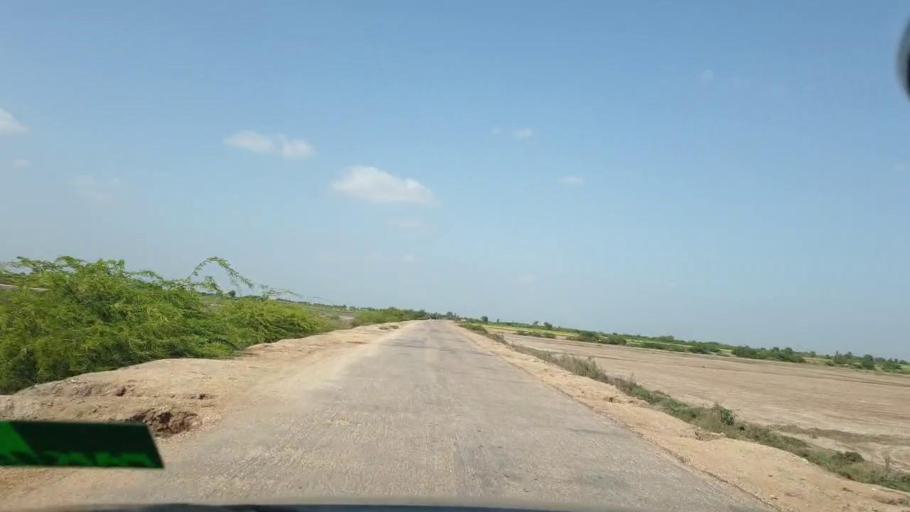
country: PK
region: Sindh
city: Tando Bago
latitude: 24.6982
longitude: 69.1903
